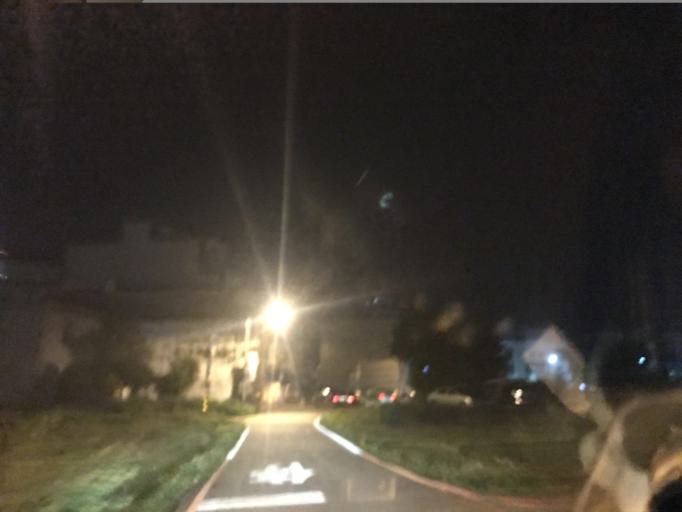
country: TW
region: Taiwan
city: Daxi
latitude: 24.8619
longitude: 121.2122
